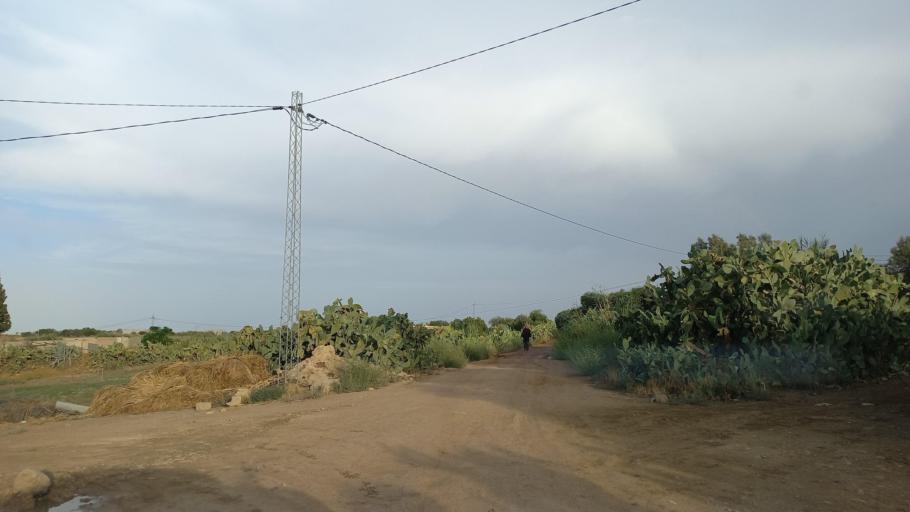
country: TN
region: Al Qasrayn
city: Kasserine
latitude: 35.2177
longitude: 9.0539
